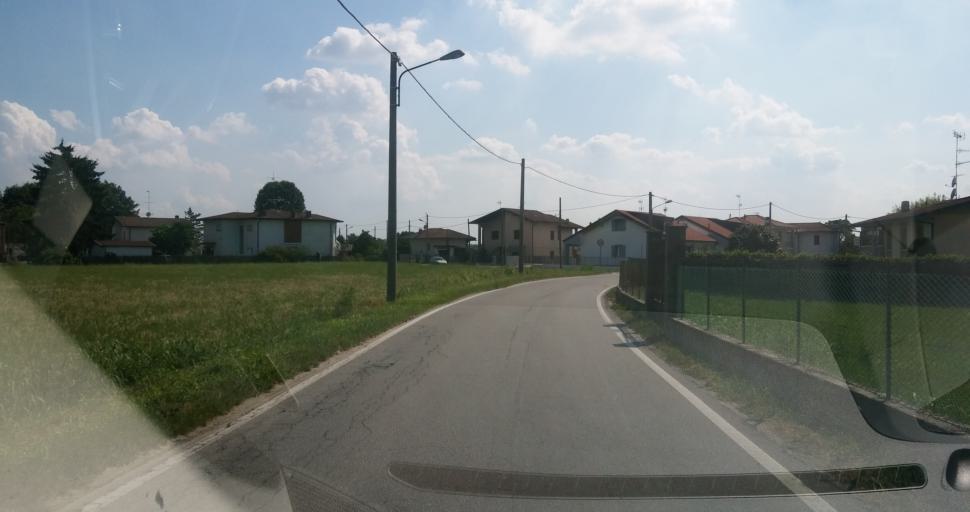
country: IT
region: Lombardy
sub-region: Provincia di Varese
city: Mercallo
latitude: 45.7315
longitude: 8.6575
